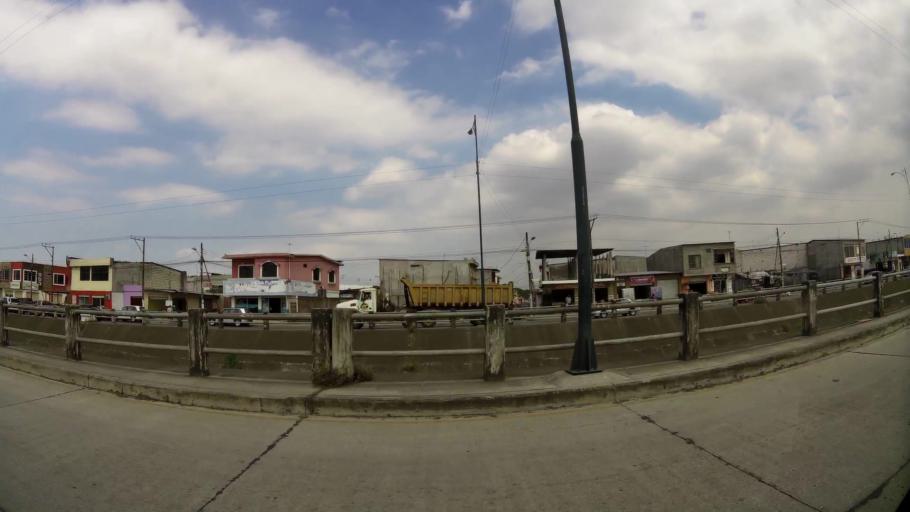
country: EC
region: Guayas
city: Eloy Alfaro
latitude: -2.0860
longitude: -79.9223
